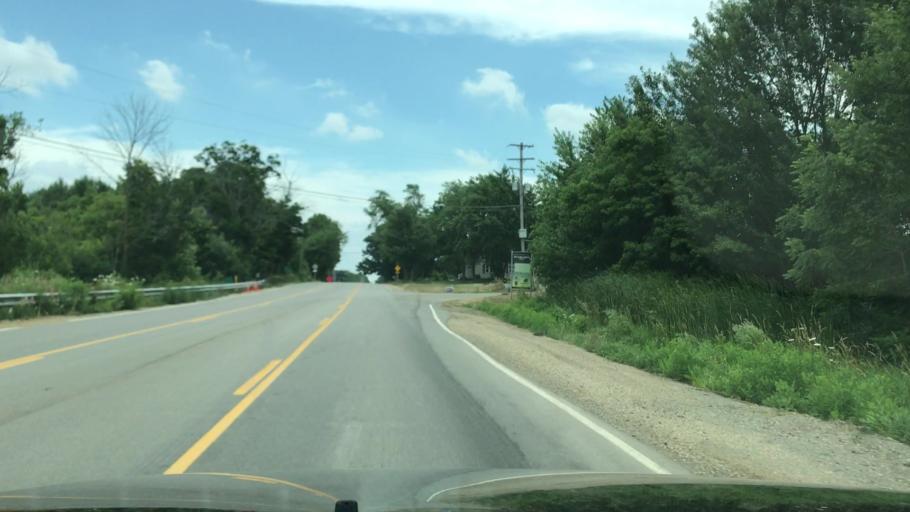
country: US
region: Michigan
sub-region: Ottawa County
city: Zeeland
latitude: 42.7831
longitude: -85.9516
